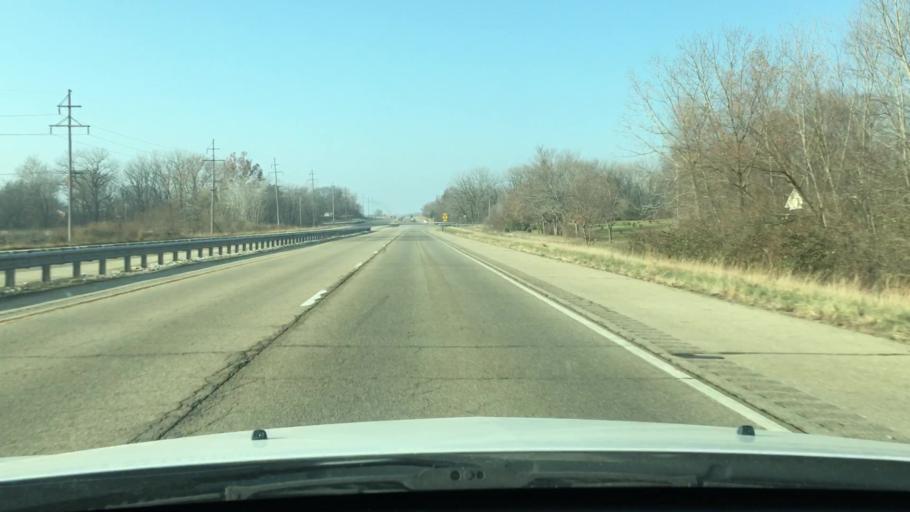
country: US
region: Illinois
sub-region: Tazewell County
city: Pekin
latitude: 40.5830
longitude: -89.6903
